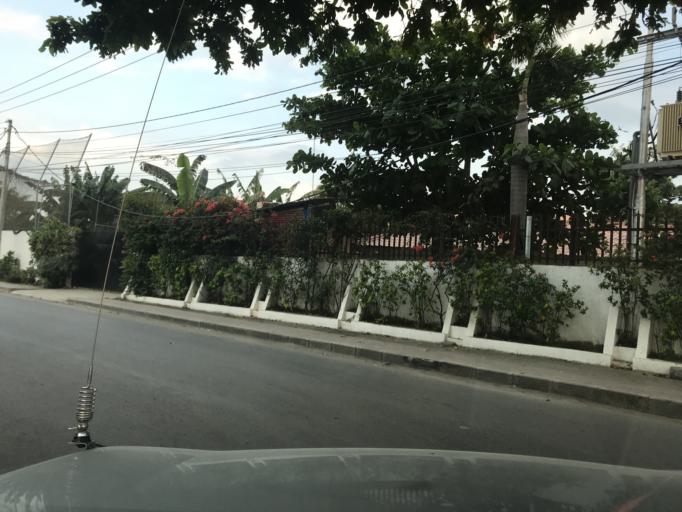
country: TL
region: Dili
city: Dili
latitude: -8.5517
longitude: 125.5432
